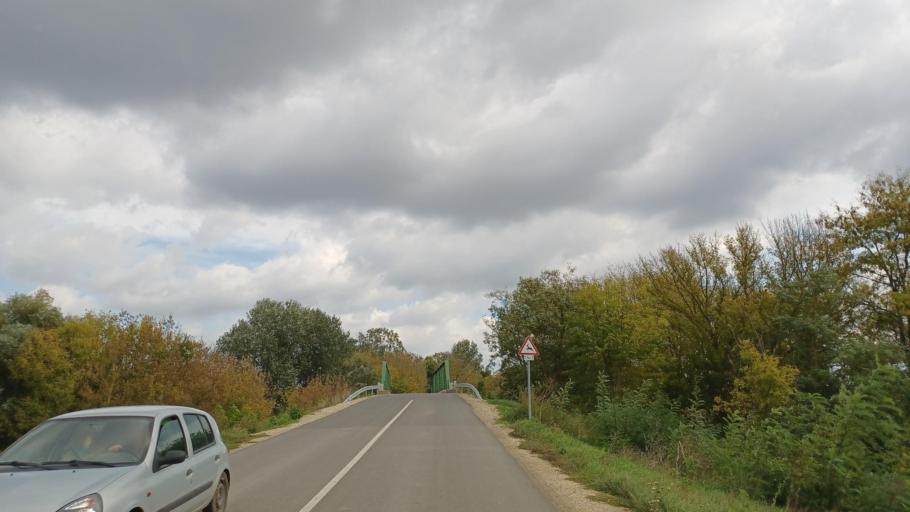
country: HU
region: Tolna
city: Nagydorog
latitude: 46.6173
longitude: 18.6096
